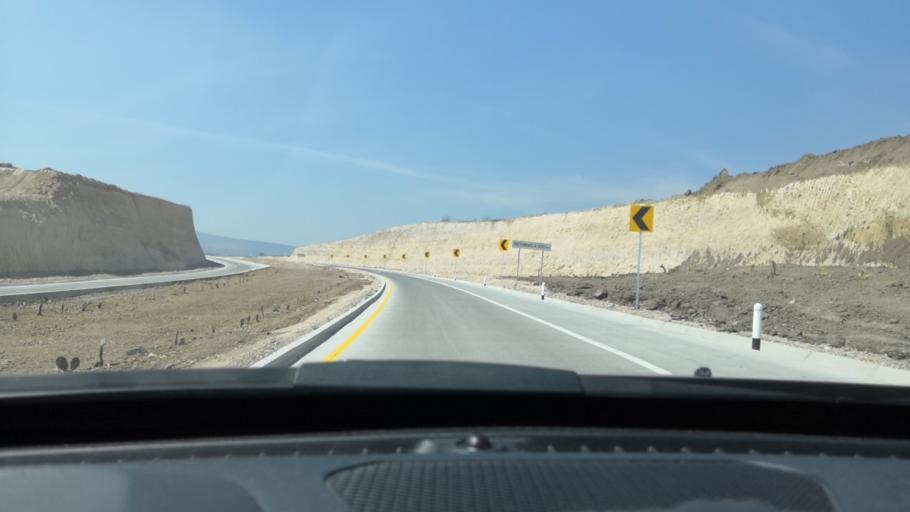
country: MX
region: Guanajuato
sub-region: Purisima del Rincon
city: Potrerillos (Guanajal)
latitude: 21.0853
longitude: -101.8556
